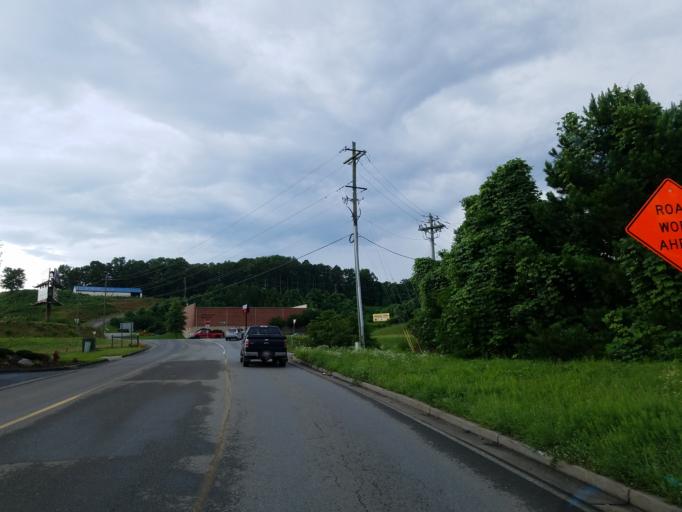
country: US
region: Georgia
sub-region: Gilmer County
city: Ellijay
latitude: 34.6643
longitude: -84.4871
